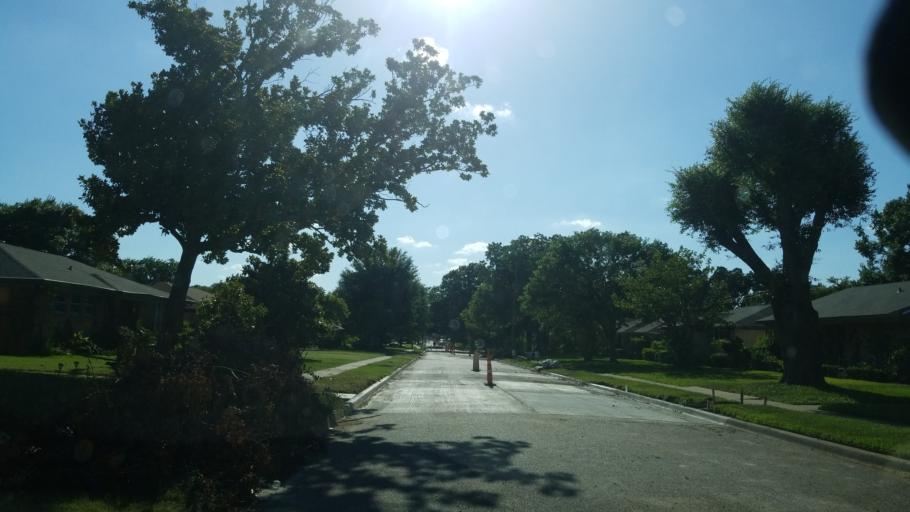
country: US
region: Texas
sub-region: Dallas County
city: Highland Park
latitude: 32.7904
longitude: -96.7030
